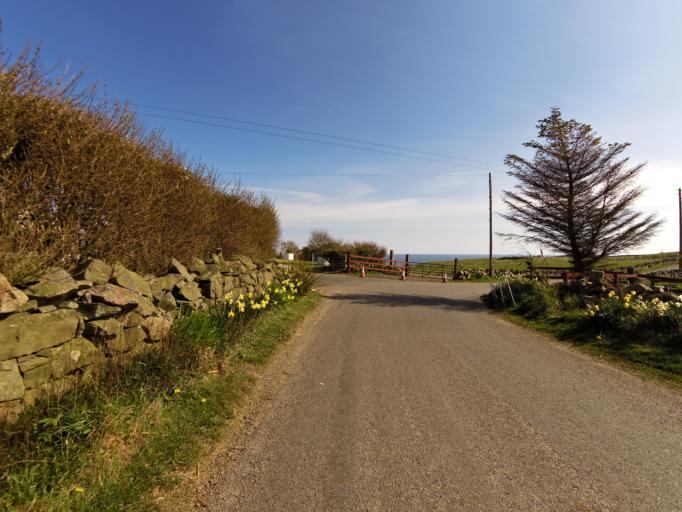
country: GB
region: Scotland
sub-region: Aberdeenshire
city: Portlethen
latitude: 57.0805
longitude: -2.0988
